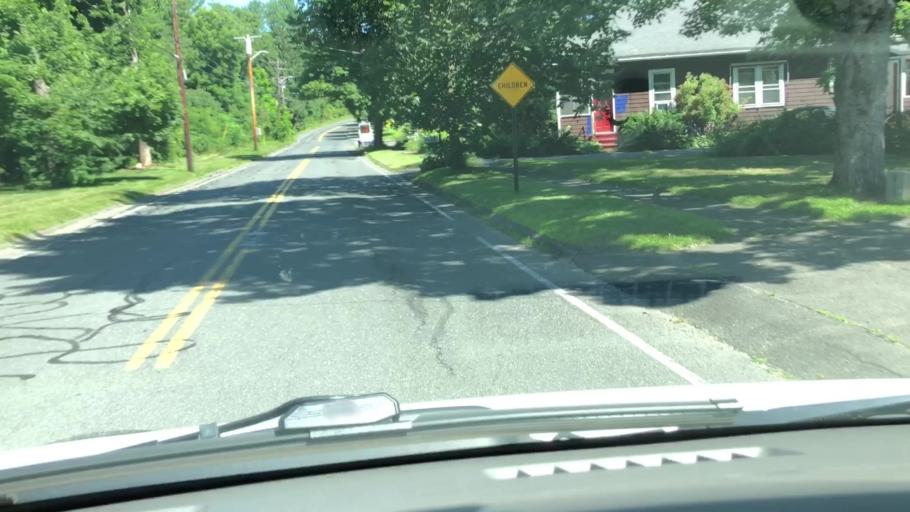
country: US
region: Massachusetts
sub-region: Hampshire County
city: Northampton
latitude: 42.3270
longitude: -72.6540
